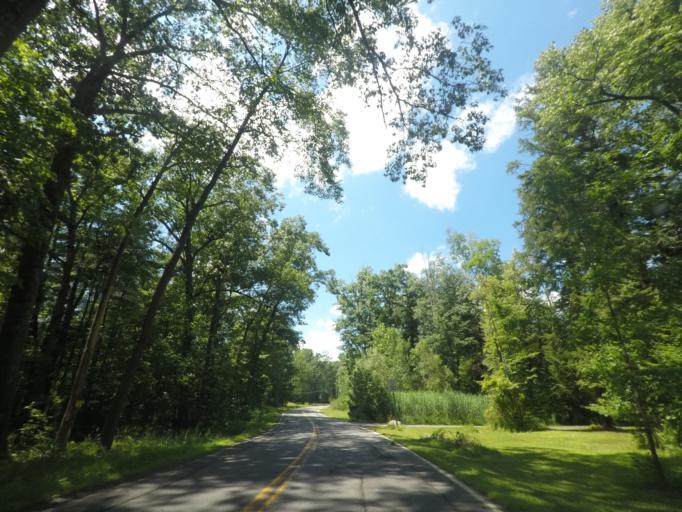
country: US
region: New York
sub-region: Albany County
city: Westmere
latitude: 42.6909
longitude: -73.9089
